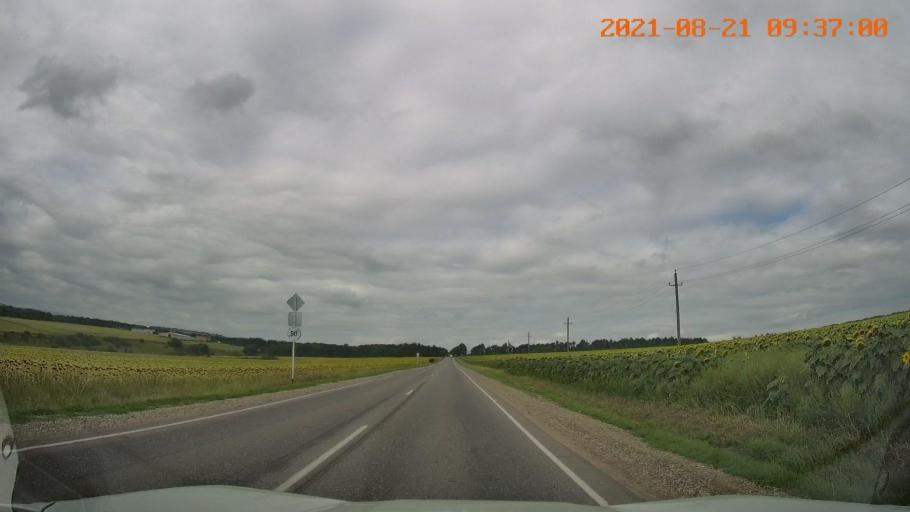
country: RU
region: Stavropol'skiy
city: Yutsa
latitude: 43.9798
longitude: 42.9440
